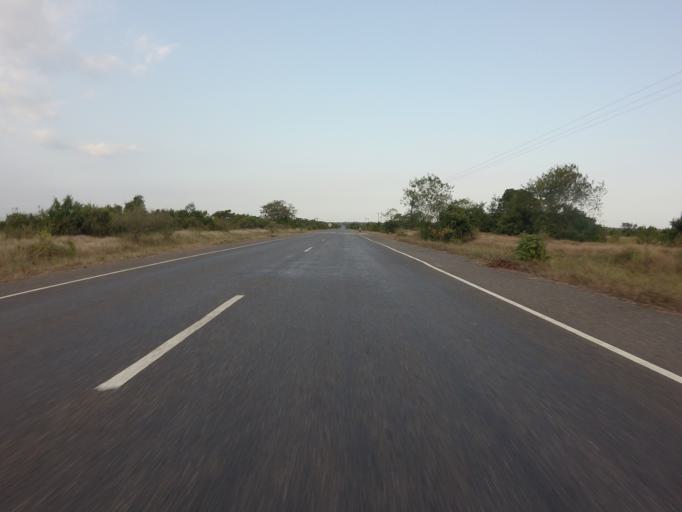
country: GH
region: Volta
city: Anloga
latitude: 6.0794
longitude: 0.5837
